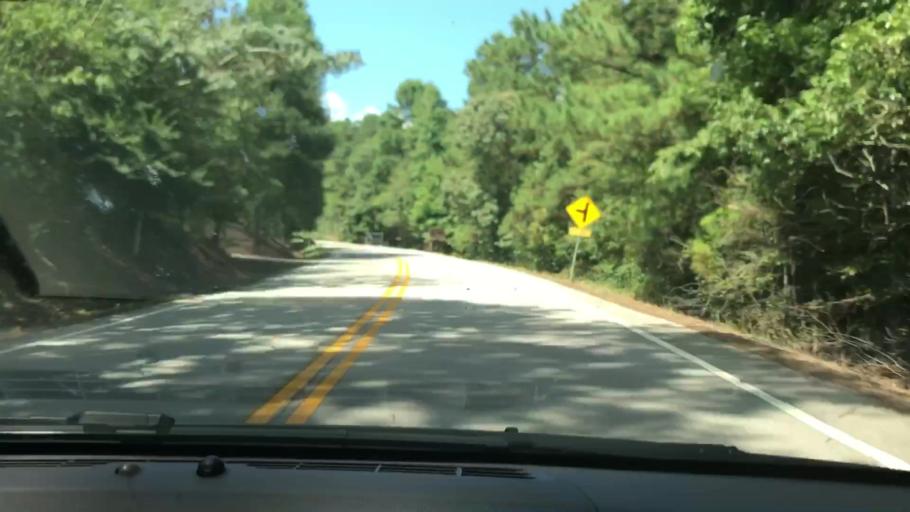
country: US
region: Georgia
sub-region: Troup County
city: La Grange
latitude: 33.1415
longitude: -85.0888
